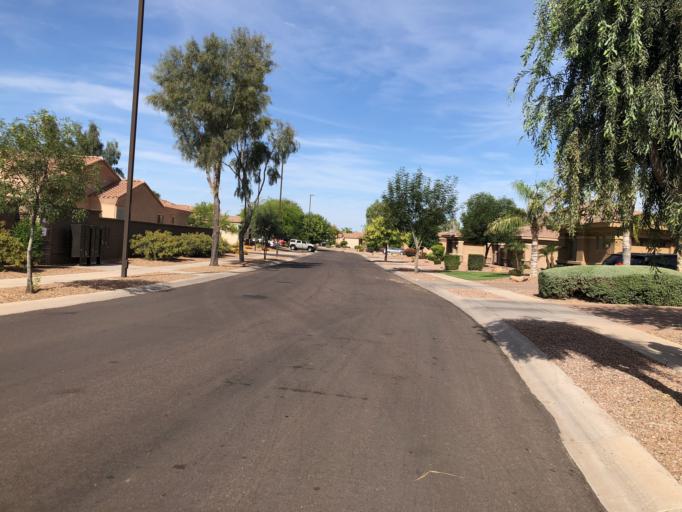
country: US
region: Arizona
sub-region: Maricopa County
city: Queen Creek
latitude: 33.2748
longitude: -111.6910
